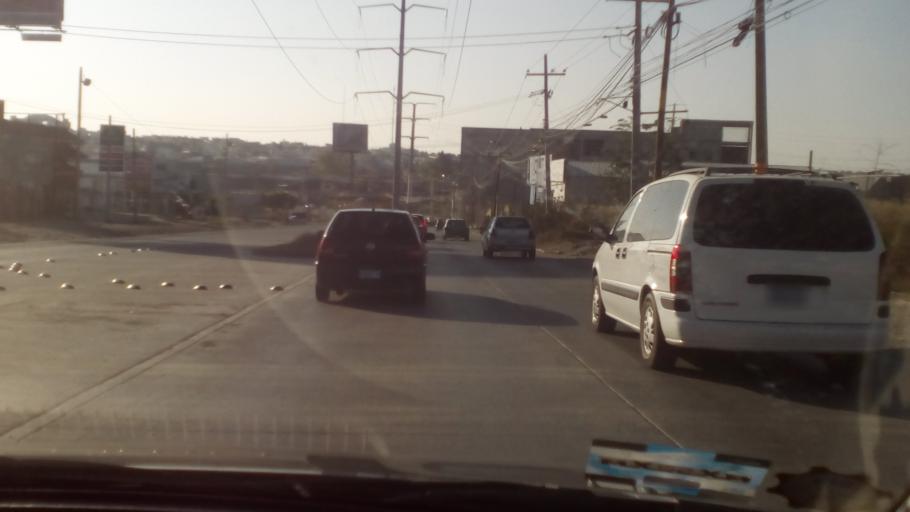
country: MX
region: Guanajuato
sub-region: Leon
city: Ejido la Joya
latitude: 21.1381
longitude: -101.7243
